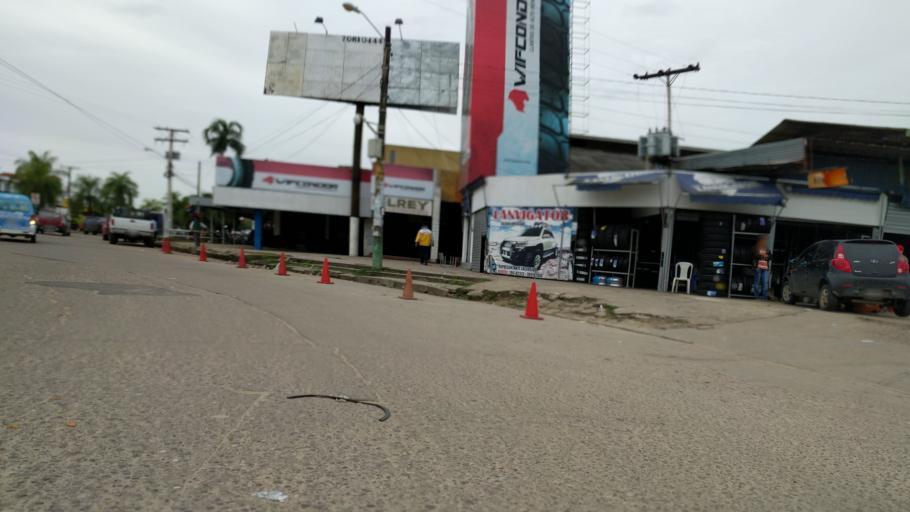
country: BO
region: Santa Cruz
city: Santa Cruz de la Sierra
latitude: -17.7905
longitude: -63.2067
